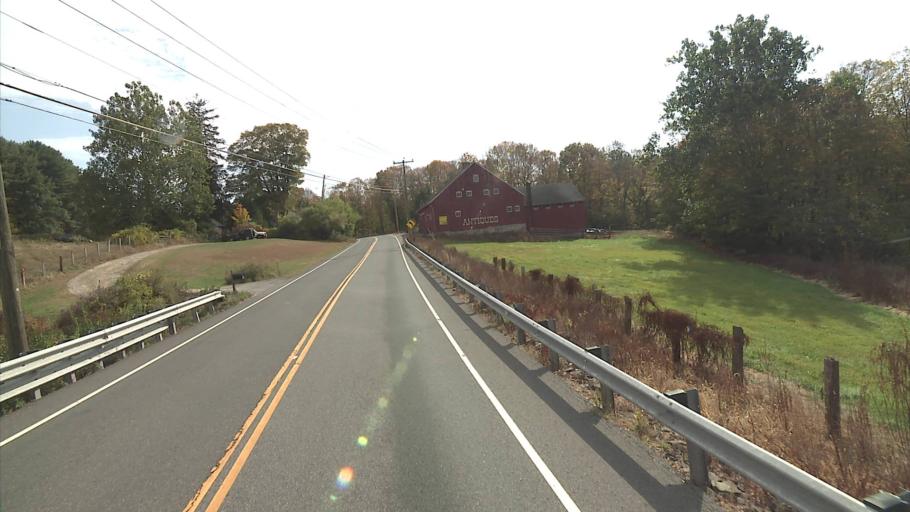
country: US
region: Connecticut
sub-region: Litchfield County
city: Woodbury Center
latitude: 41.5746
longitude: -73.1855
